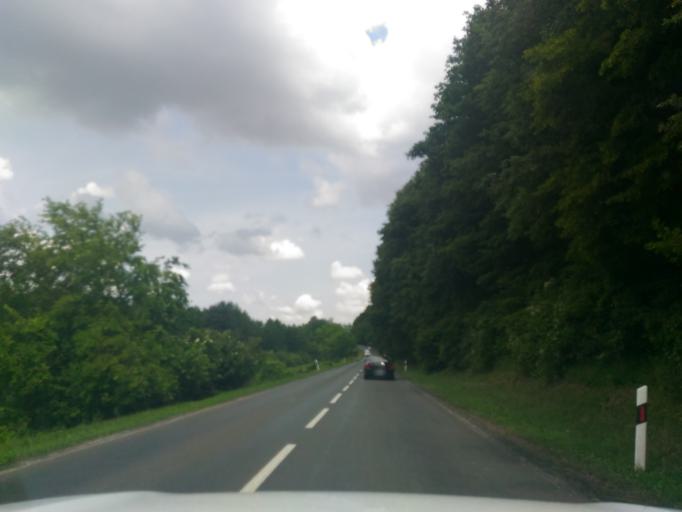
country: HU
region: Baranya
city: Komlo
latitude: 46.1727
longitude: 18.2119
